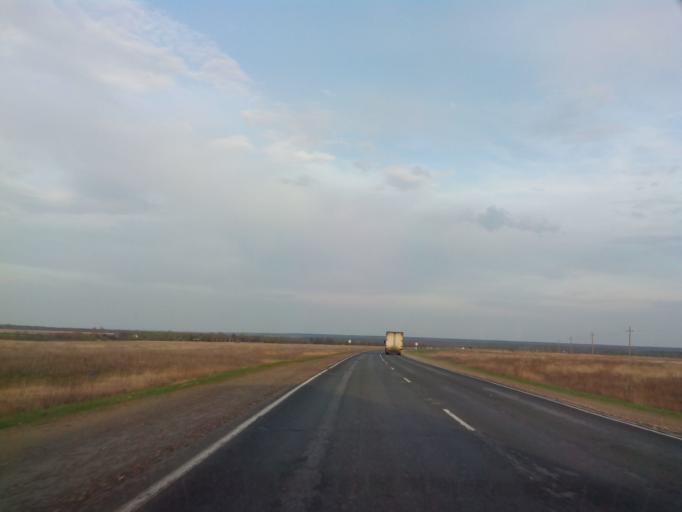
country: RU
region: Rjazan
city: Korablino
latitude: 53.7457
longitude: 39.8763
